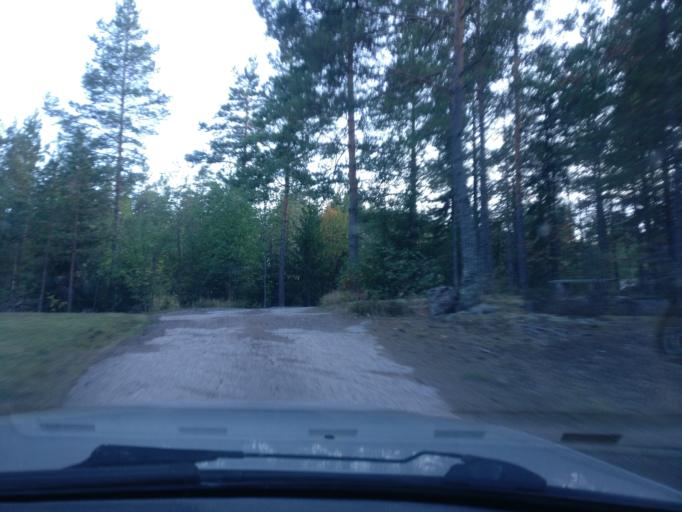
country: FI
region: Kymenlaakso
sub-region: Kotka-Hamina
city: Broby
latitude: 60.4719
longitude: 26.7756
